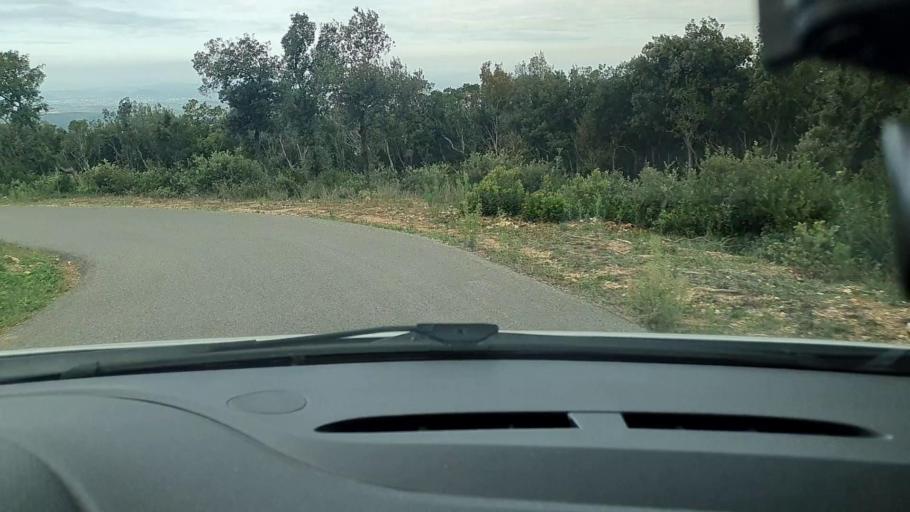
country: FR
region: Languedoc-Roussillon
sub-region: Departement du Gard
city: Mons
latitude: 44.1393
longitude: 4.2752
